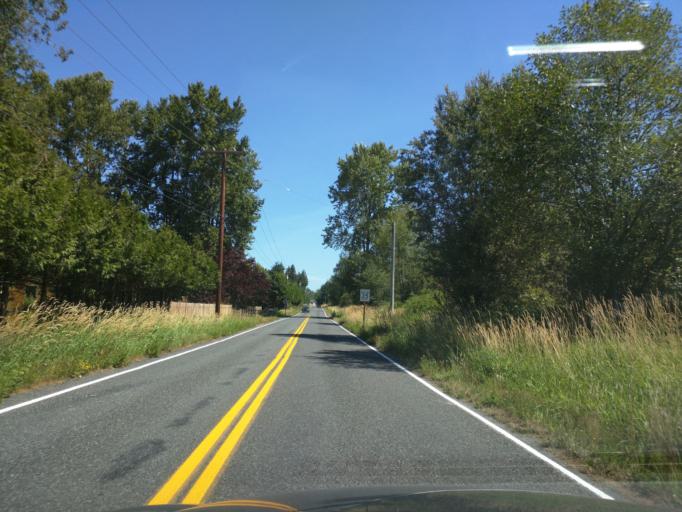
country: US
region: Washington
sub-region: Whatcom County
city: Geneva
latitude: 48.7898
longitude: -122.4333
